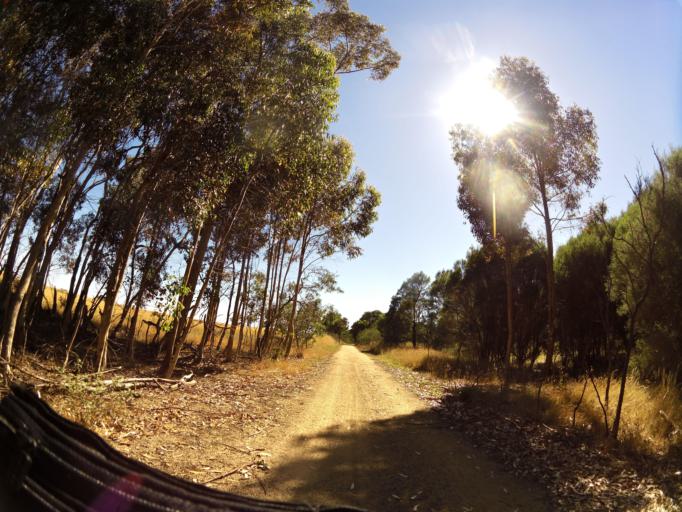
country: AU
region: Victoria
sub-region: Ballarat North
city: Delacombe
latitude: -37.6713
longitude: 143.4525
